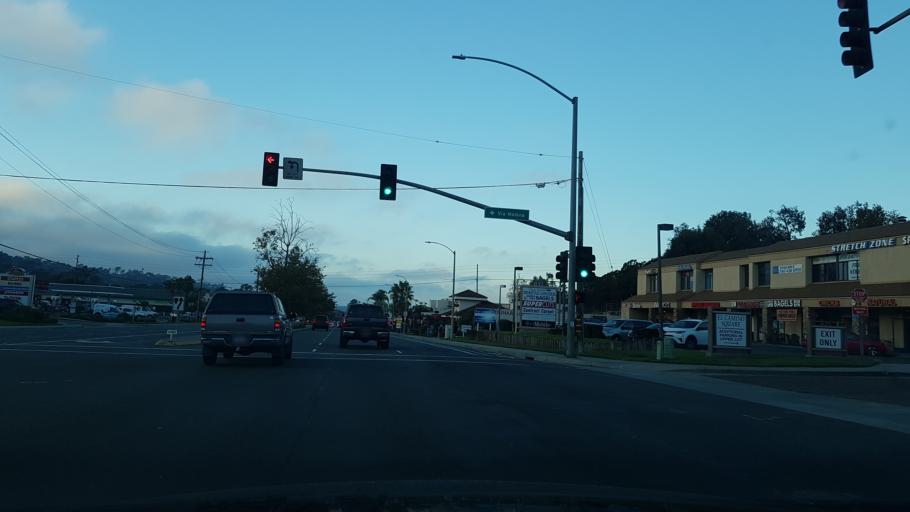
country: US
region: California
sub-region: San Diego County
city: Encinitas
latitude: 33.0485
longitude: -117.2596
